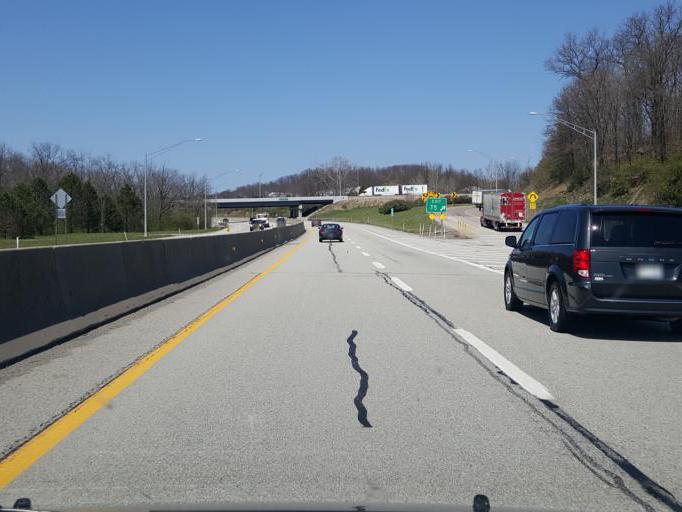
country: US
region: Pennsylvania
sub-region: Westmoreland County
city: New Stanton
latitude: 40.2218
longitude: -79.6041
